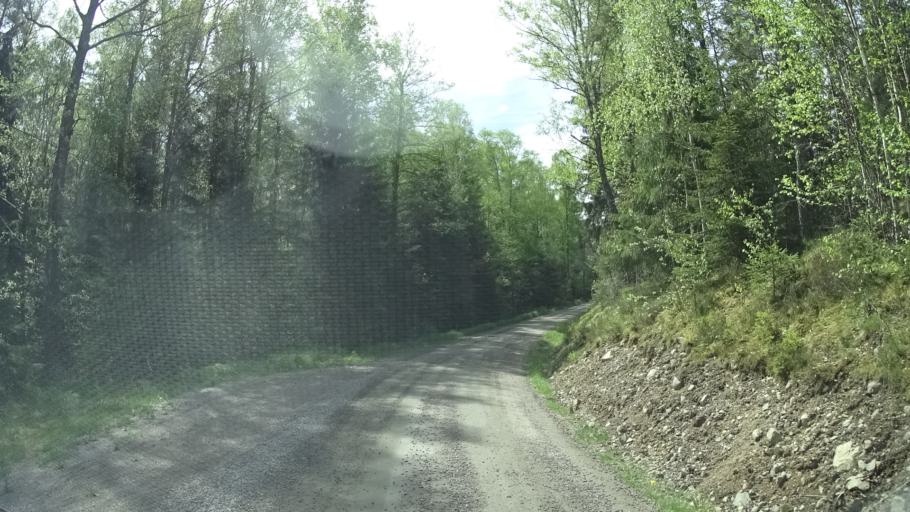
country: SE
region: OEstergoetland
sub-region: Finspangs Kommun
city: Finspang
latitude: 58.7650
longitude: 15.8363
